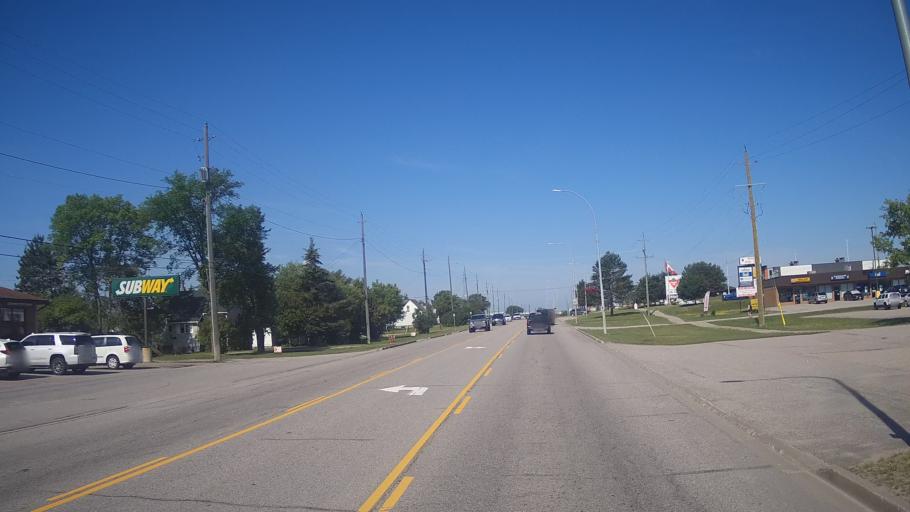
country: CA
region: Ontario
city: Dryden
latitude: 49.7863
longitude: -92.8257
